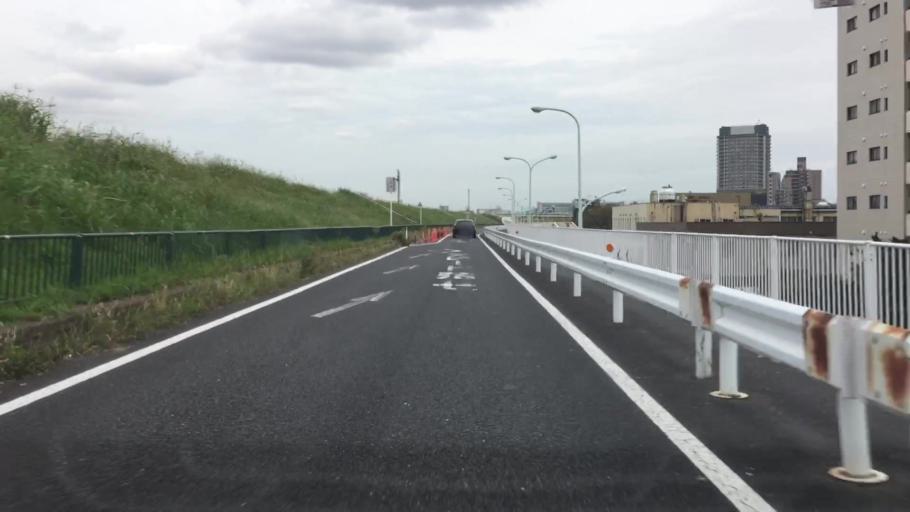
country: JP
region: Saitama
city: Soka
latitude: 35.7570
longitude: 139.7936
